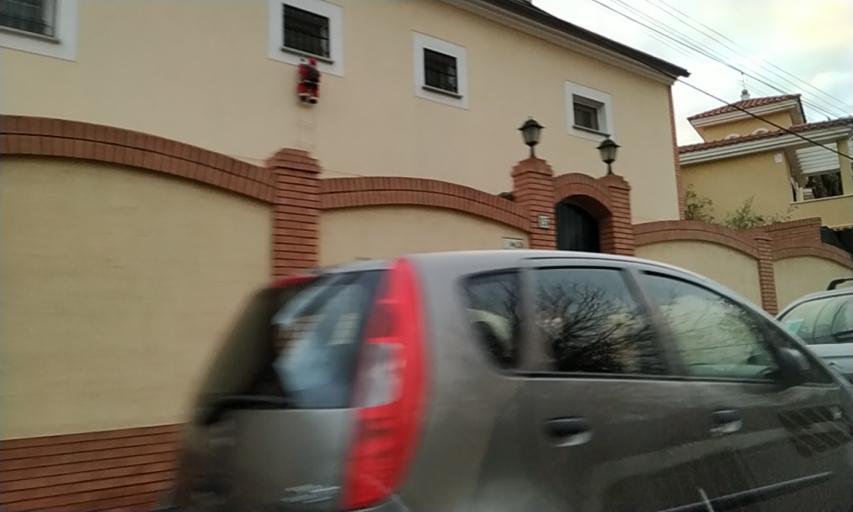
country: ES
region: Extremadura
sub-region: Provincia de Badajoz
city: Badajoz
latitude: 38.8853
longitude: -6.9875
